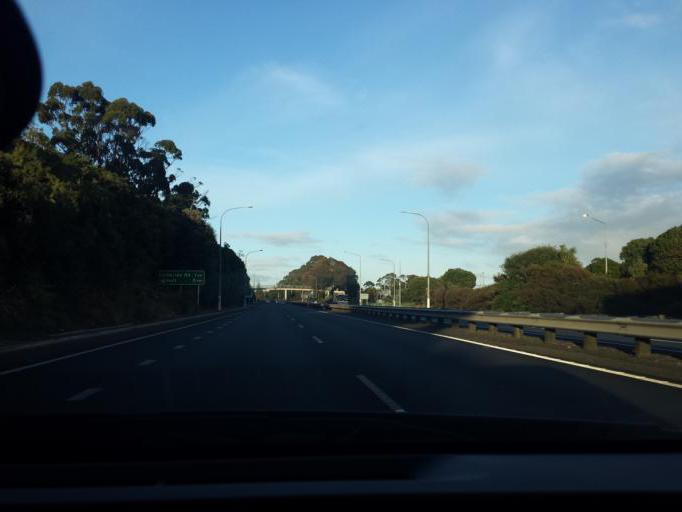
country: NZ
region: Auckland
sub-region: Auckland
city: Mangere
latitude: -36.9666
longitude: 174.7963
